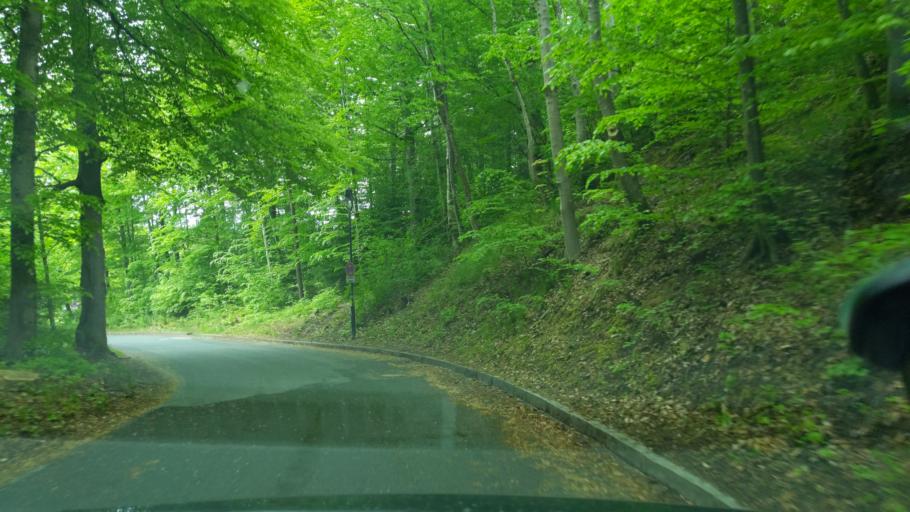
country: DE
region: Bavaria
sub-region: Upper Bavaria
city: Ebersberg
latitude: 48.0940
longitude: 11.9595
